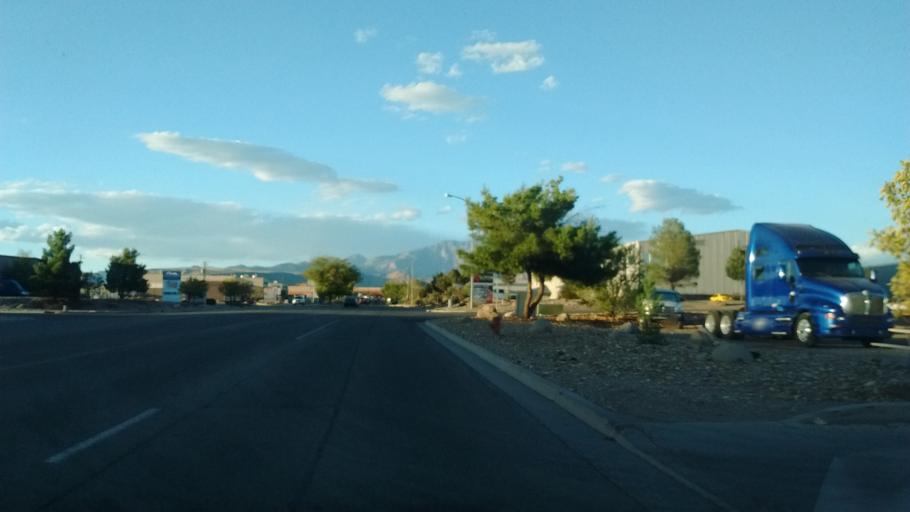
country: US
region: Utah
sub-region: Washington County
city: Washington
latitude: 37.1162
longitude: -113.5206
